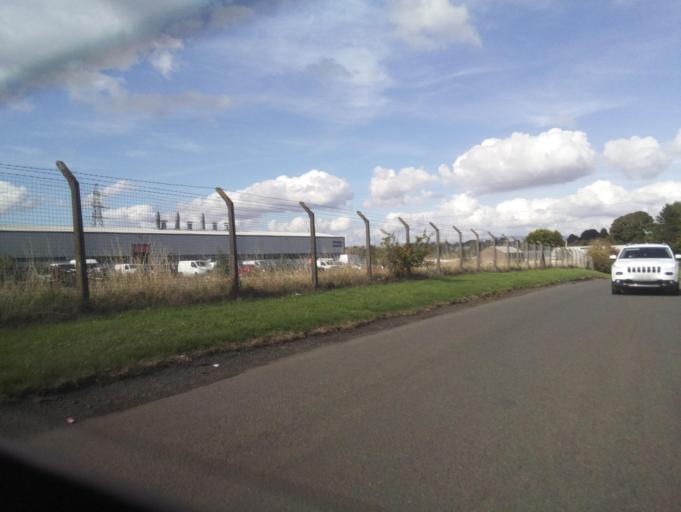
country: GB
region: Scotland
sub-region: Falkirk
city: Larbert
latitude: 56.0141
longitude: -3.8342
